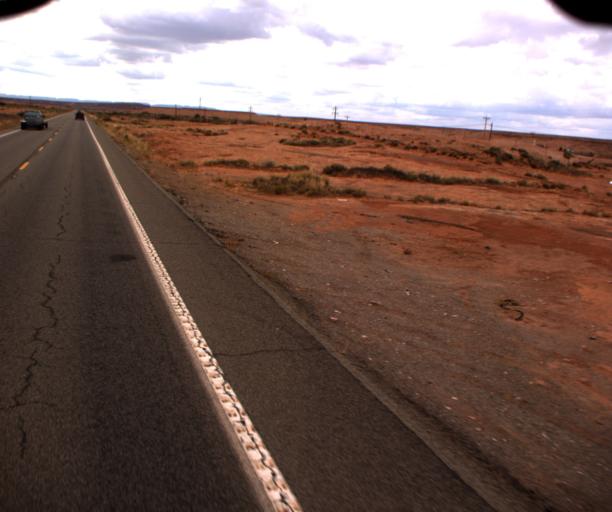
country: US
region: Arizona
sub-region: Navajo County
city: Kayenta
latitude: 36.8325
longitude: -109.8557
